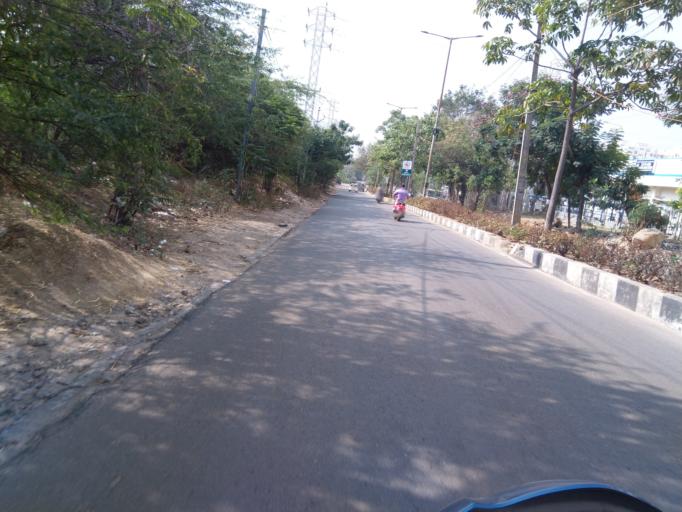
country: IN
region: Telangana
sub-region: Rangareddi
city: Kukatpalli
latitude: 17.4737
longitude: 78.3940
